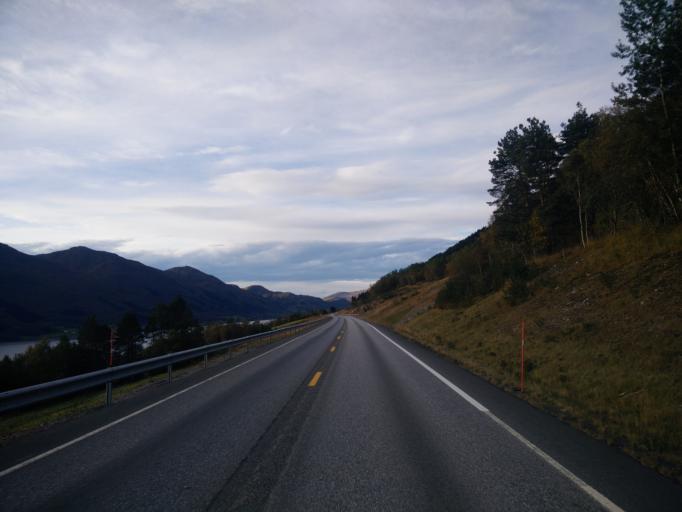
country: NO
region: More og Romsdal
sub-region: Gjemnes
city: Batnfjordsora
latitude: 62.9416
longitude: 7.7403
